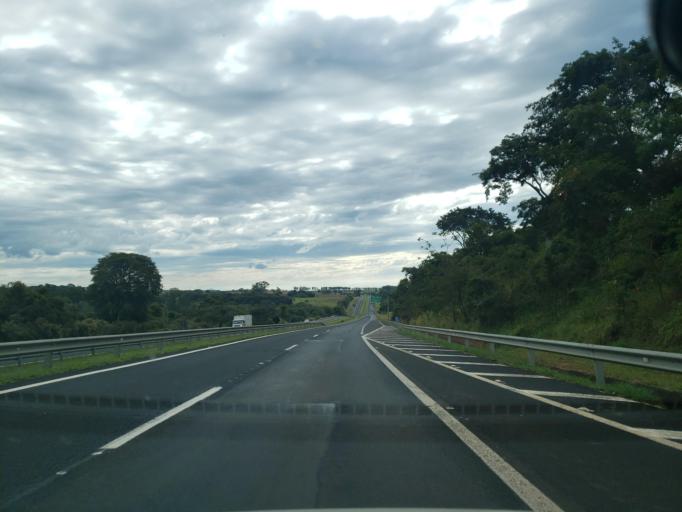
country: BR
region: Sao Paulo
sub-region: Bauru
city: Bauru
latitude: -22.2094
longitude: -49.1808
